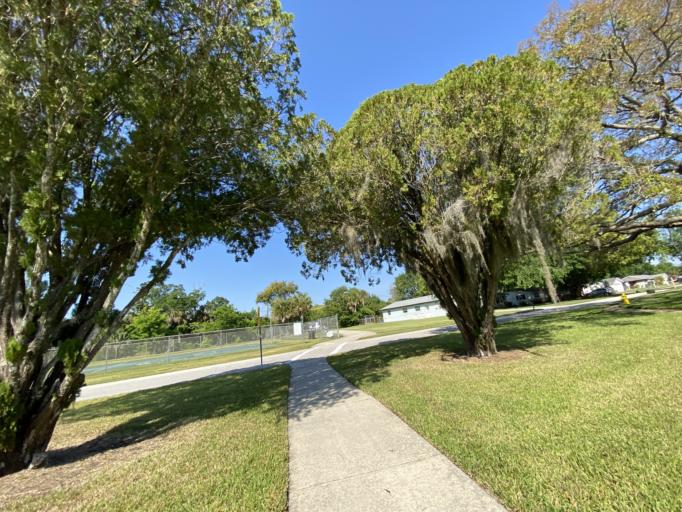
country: US
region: Florida
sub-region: Volusia County
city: South Daytona
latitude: 29.1671
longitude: -81.0104
